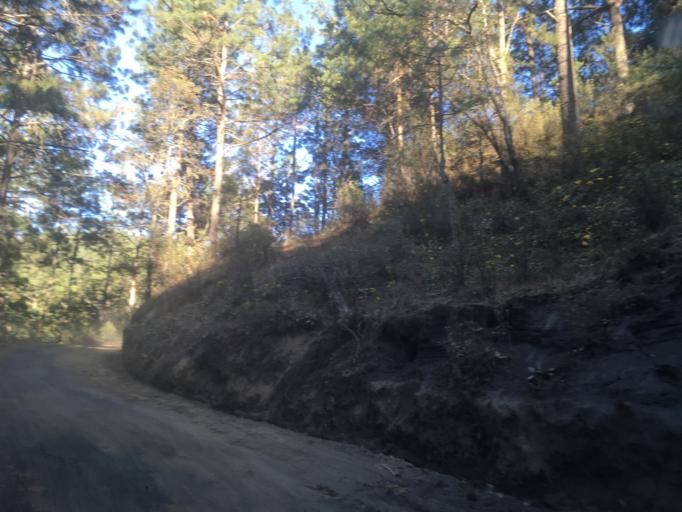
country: MX
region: Michoacan
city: Angahuan
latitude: 19.4740
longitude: -102.2423
